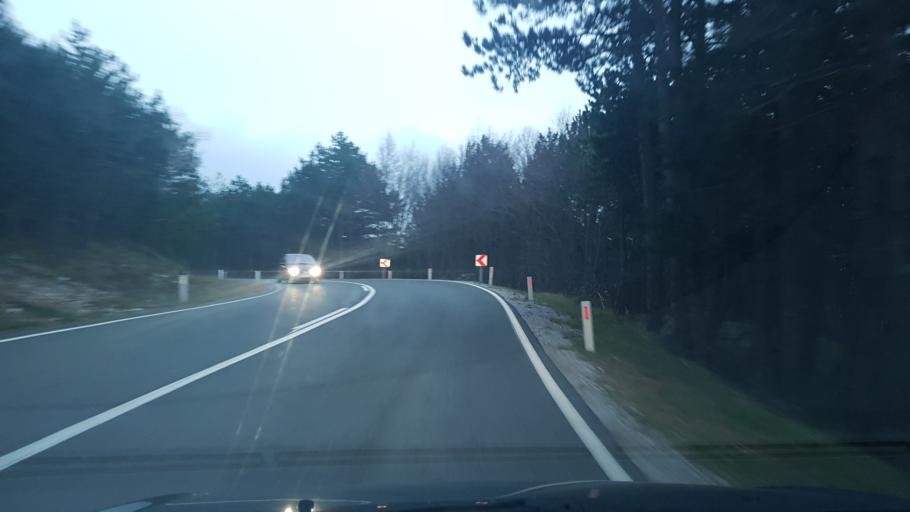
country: SI
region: Vipava
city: Vipava
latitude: 45.8803
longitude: 13.9540
